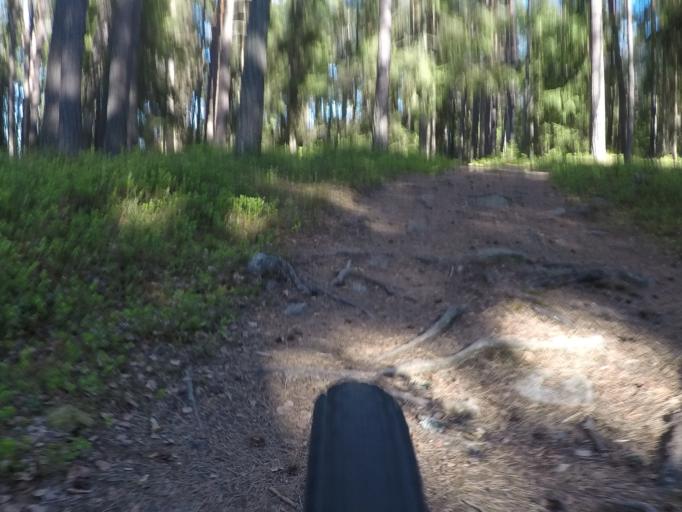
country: SE
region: Soedermanland
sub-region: Eskilstuna Kommun
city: Eskilstuna
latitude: 59.4002
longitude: 16.5400
